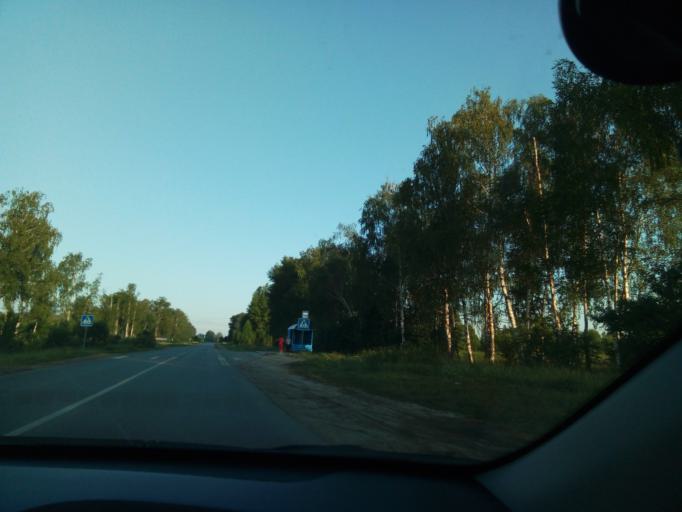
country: RU
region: Nizjnij Novgorod
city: Satis
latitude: 54.9383
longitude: 43.2585
